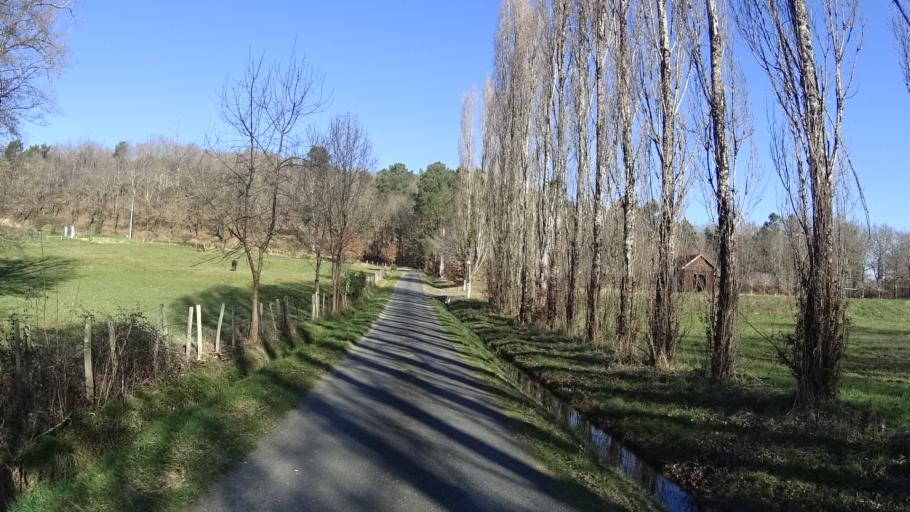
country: FR
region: Aquitaine
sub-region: Departement de la Dordogne
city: Saint-Medard-de-Mussidan
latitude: 45.0417
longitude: 0.2568
